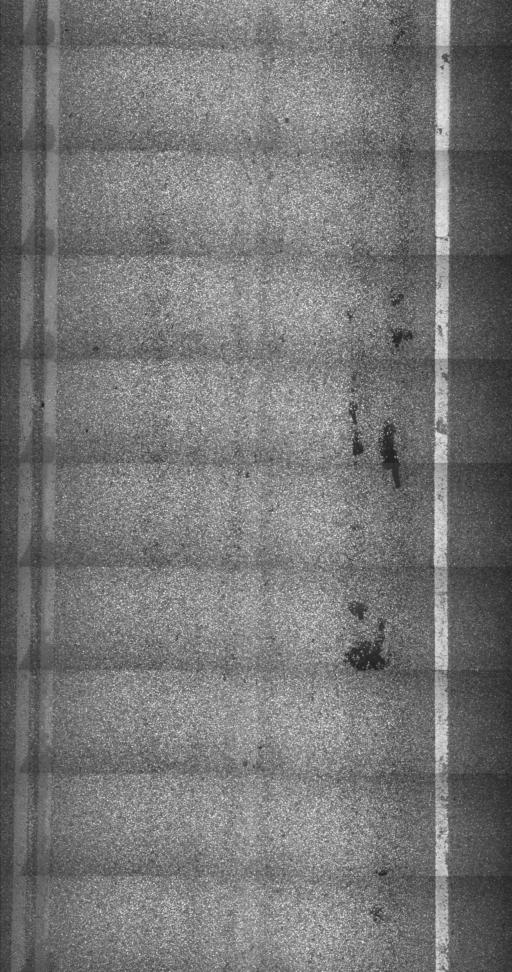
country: US
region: New York
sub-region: Clinton County
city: Rouses Point
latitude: 44.9595
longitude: -73.2768
